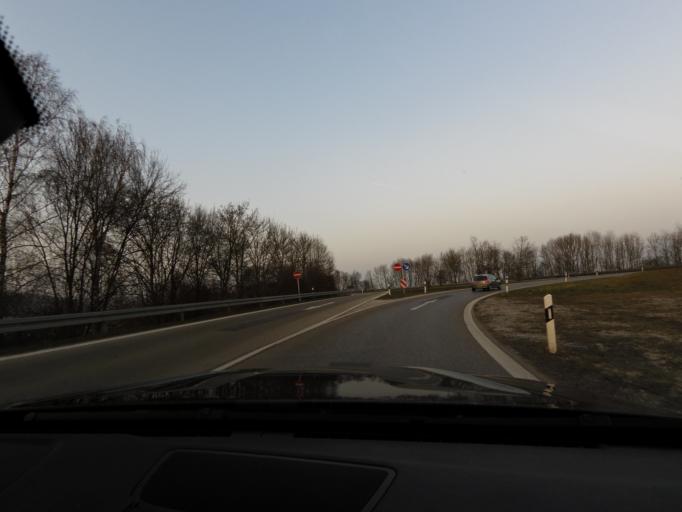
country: DE
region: Bavaria
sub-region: Lower Bavaria
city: Eching
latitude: 48.5342
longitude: 12.0704
